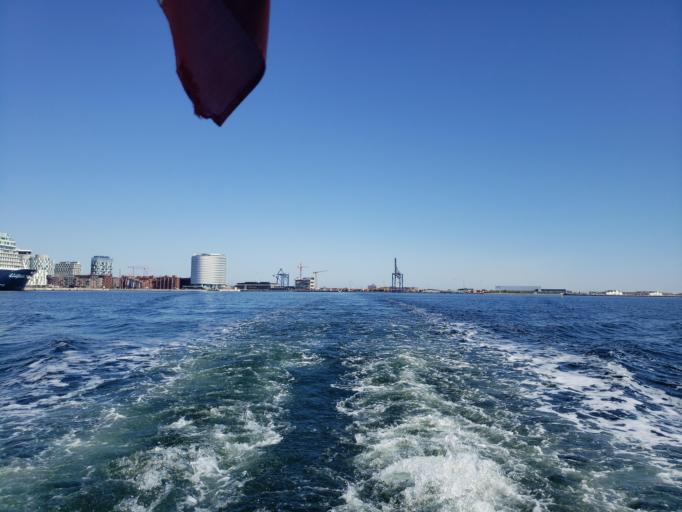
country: DK
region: Capital Region
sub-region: Kobenhavn
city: Christianshavn
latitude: 55.6985
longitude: 12.6053
